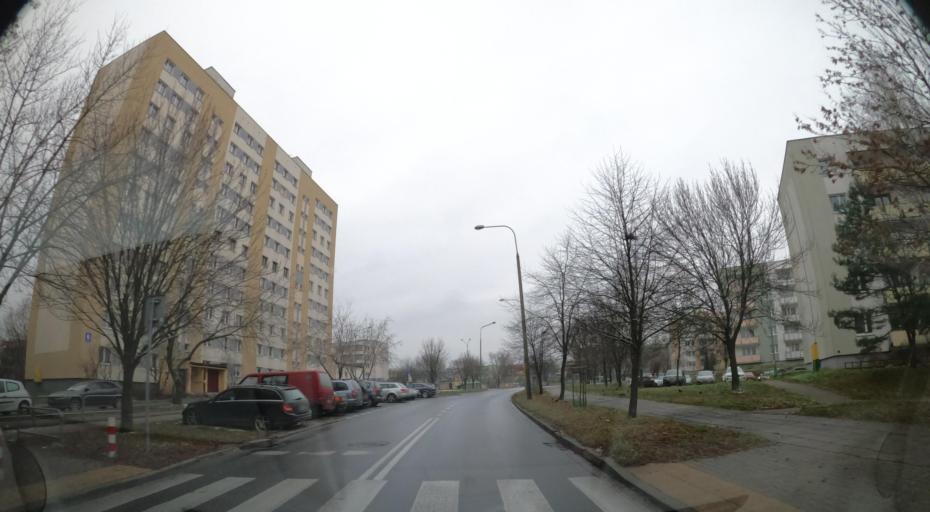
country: PL
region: Masovian Voivodeship
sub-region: Powiat radomski
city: Trablice
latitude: 51.3705
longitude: 21.1348
